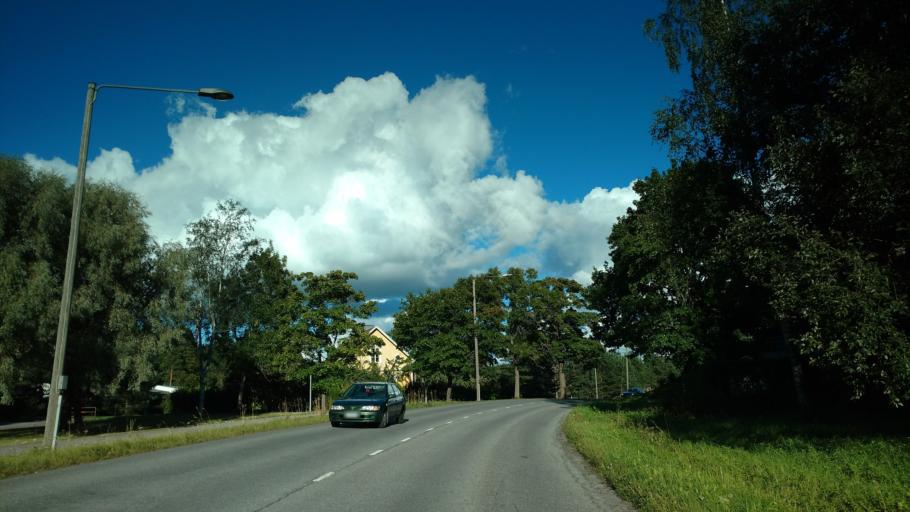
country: FI
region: Varsinais-Suomi
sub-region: Salo
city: Halikko
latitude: 60.3967
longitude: 23.0982
